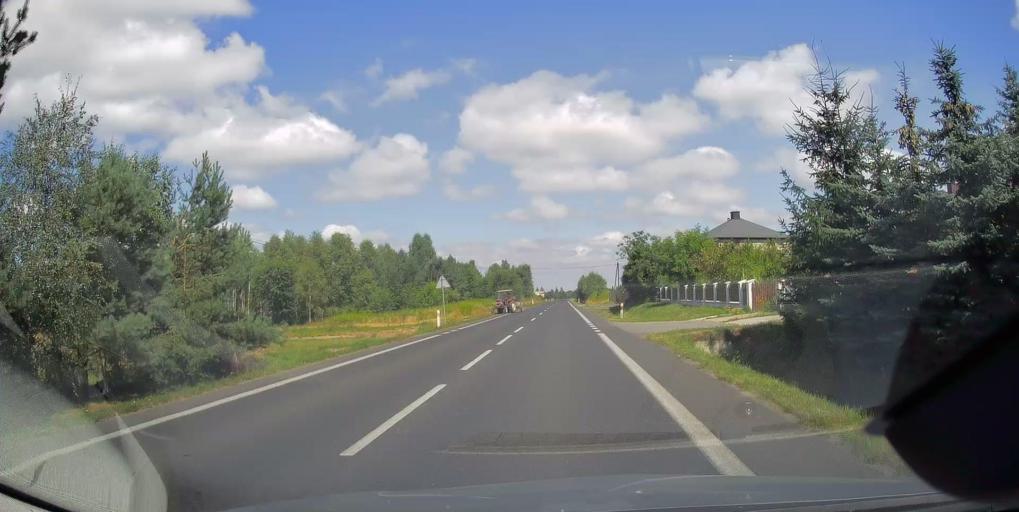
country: PL
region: Subcarpathian Voivodeship
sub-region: Powiat debicki
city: Brzeznica
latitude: 50.1349
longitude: 21.4852
